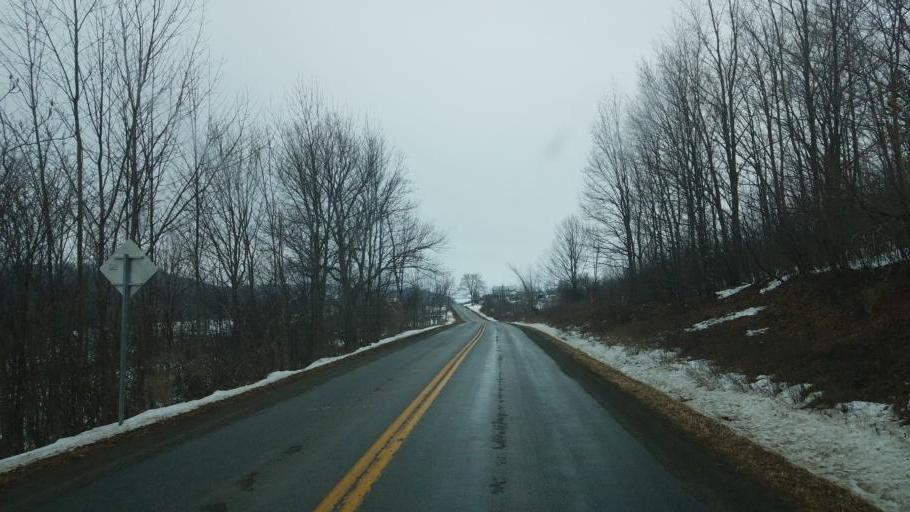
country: US
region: Pennsylvania
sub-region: Tioga County
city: Elkland
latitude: 42.0796
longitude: -77.4596
